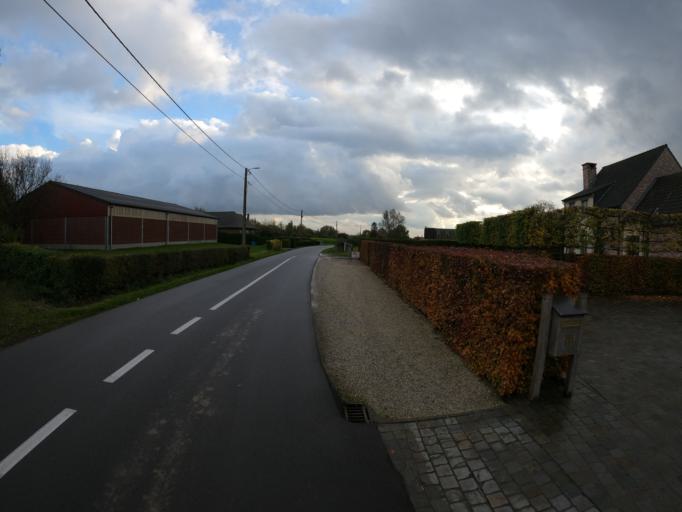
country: BE
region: Flanders
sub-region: Provincie Oost-Vlaanderen
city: Hamme
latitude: 51.1207
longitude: 4.1629
